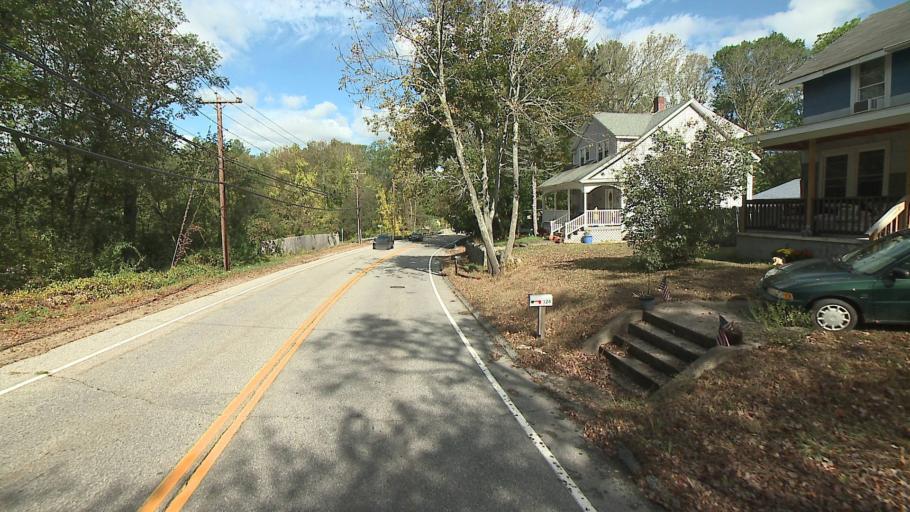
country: US
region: Connecticut
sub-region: Windham County
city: Killingly Center
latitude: 41.8629
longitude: -71.8830
